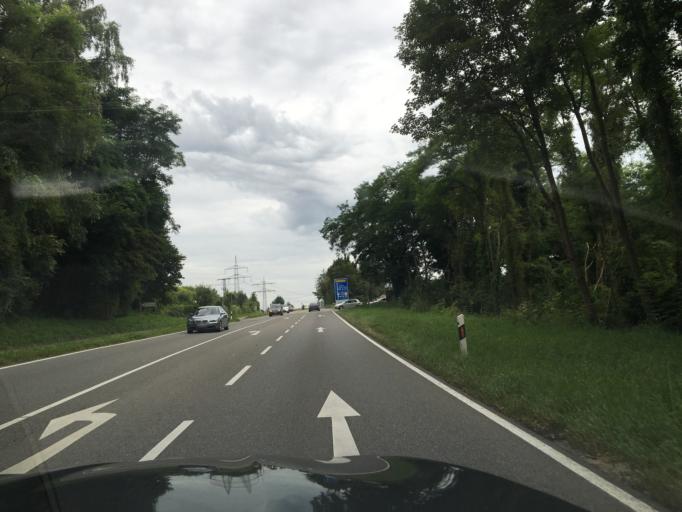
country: DE
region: Baden-Wuerttemberg
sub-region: Freiburg Region
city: Stockach
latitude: 47.8405
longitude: 8.9933
